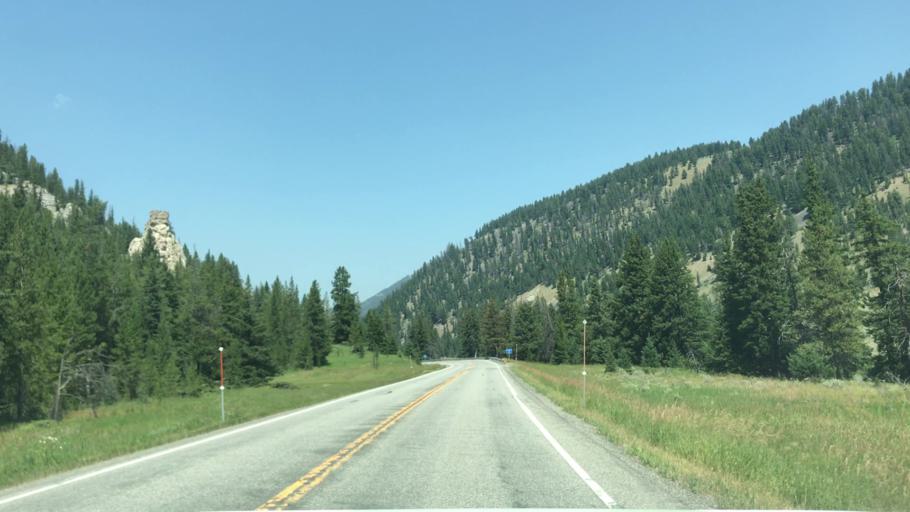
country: US
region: Montana
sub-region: Gallatin County
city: Big Sky
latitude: 45.0810
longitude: -111.2084
